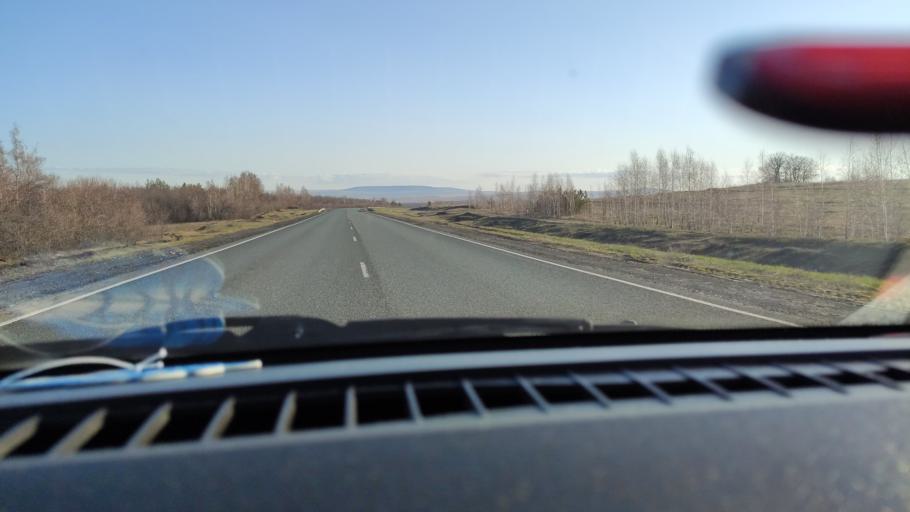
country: RU
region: Saratov
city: Balakovo
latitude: 52.1655
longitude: 47.8262
